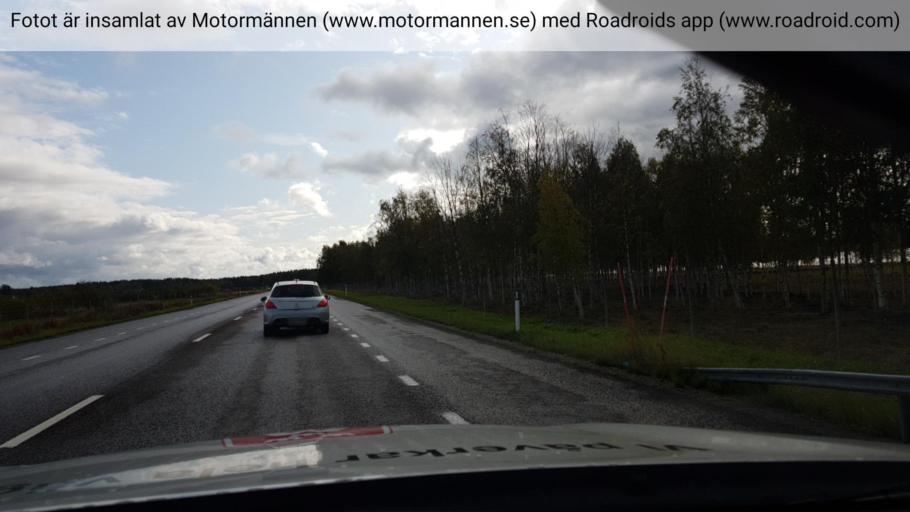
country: SE
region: Norrbotten
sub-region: Lulea Kommun
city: Sodra Sunderbyn
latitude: 65.6955
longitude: 21.8303
